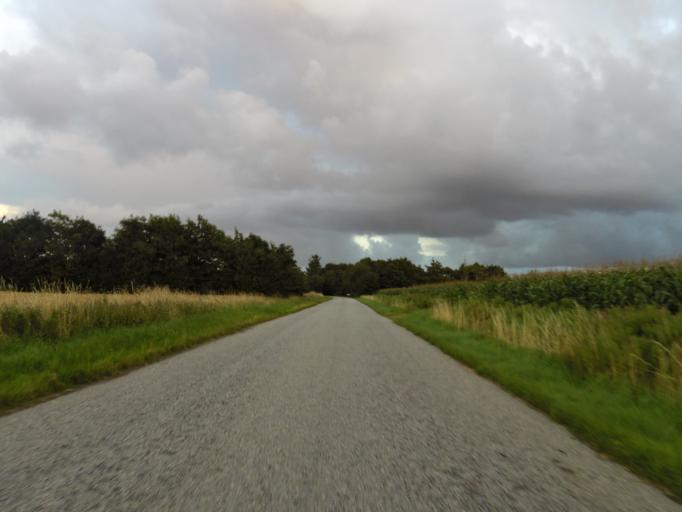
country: DK
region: South Denmark
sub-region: Esbjerg Kommune
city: Ribe
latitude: 55.2800
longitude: 8.8140
